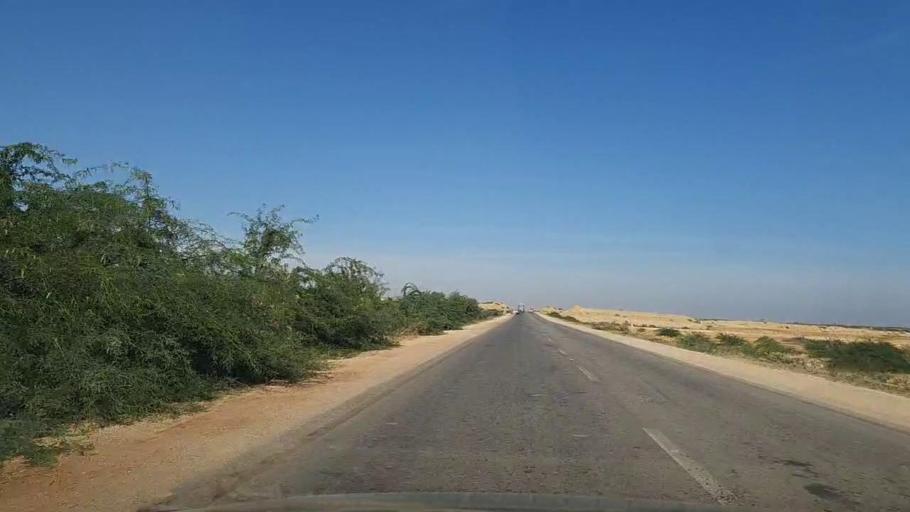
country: PK
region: Sindh
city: Kotri
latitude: 25.2081
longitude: 68.2373
